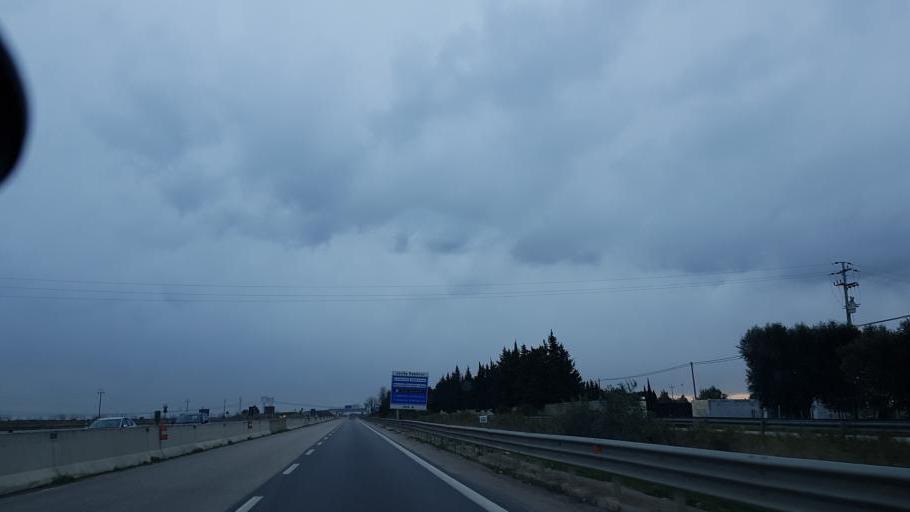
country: IT
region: Apulia
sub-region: Provincia di Brindisi
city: Brindisi
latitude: 40.6082
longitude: 17.8892
